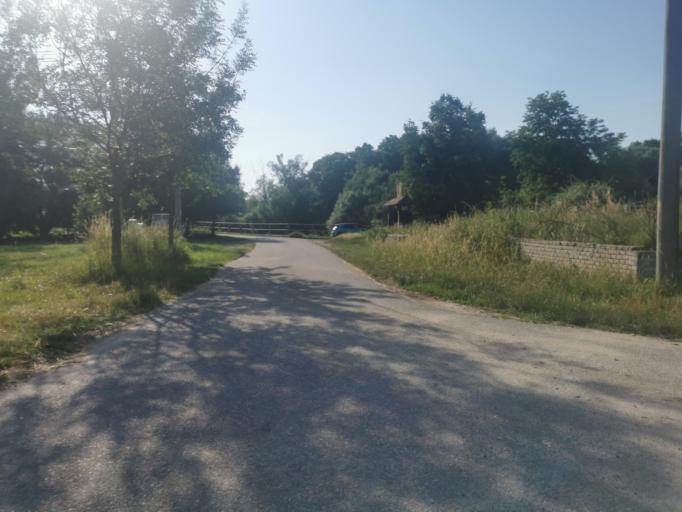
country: CZ
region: South Moravian
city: Vacenovice
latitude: 48.9238
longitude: 17.1961
